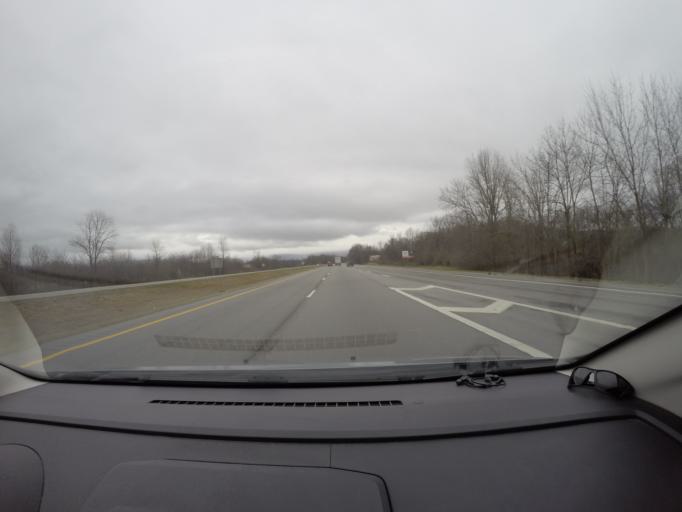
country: US
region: Tennessee
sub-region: Marion County
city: Monteagle
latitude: 35.2982
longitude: -85.9013
